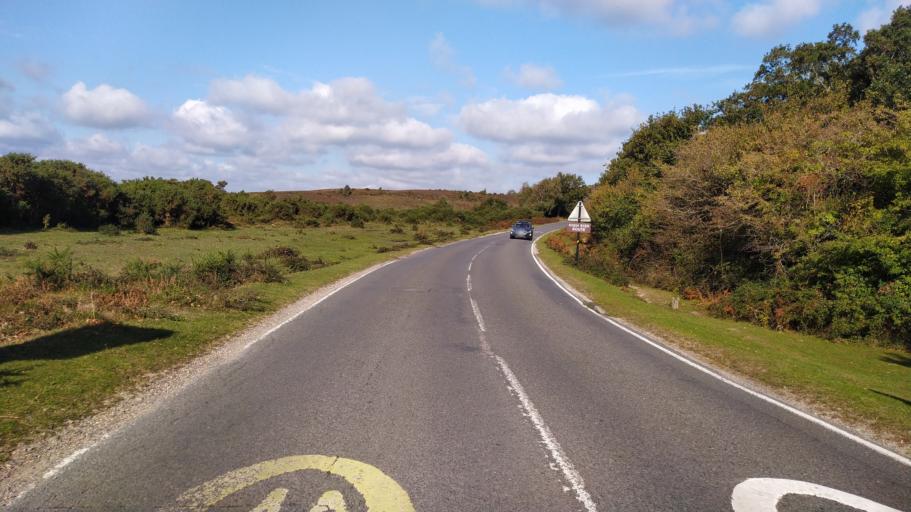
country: GB
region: England
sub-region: Hampshire
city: Bransgore
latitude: 50.8380
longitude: -1.7195
